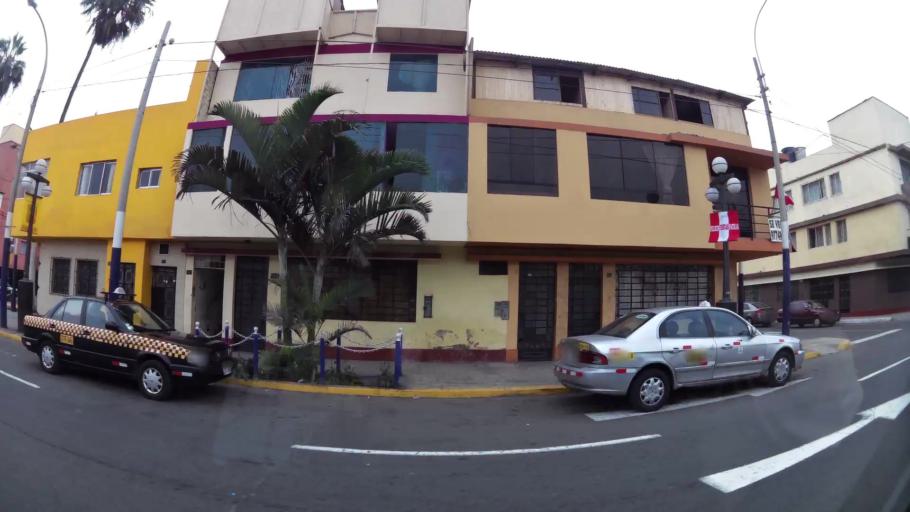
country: PE
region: Lima
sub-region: Lima
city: Surco
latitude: -12.1702
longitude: -77.0278
